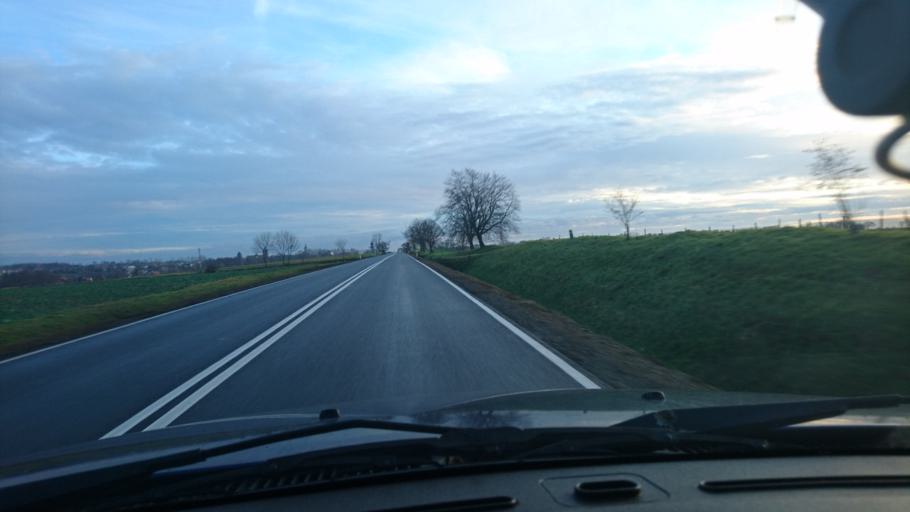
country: PL
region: Opole Voivodeship
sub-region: Powiat kluczborski
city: Byczyna
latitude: 51.1248
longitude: 18.2036
